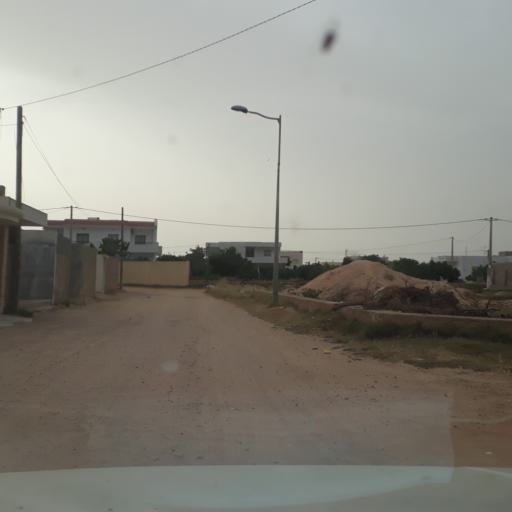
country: TN
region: Safaqis
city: Al Qarmadah
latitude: 34.8186
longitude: 10.7727
